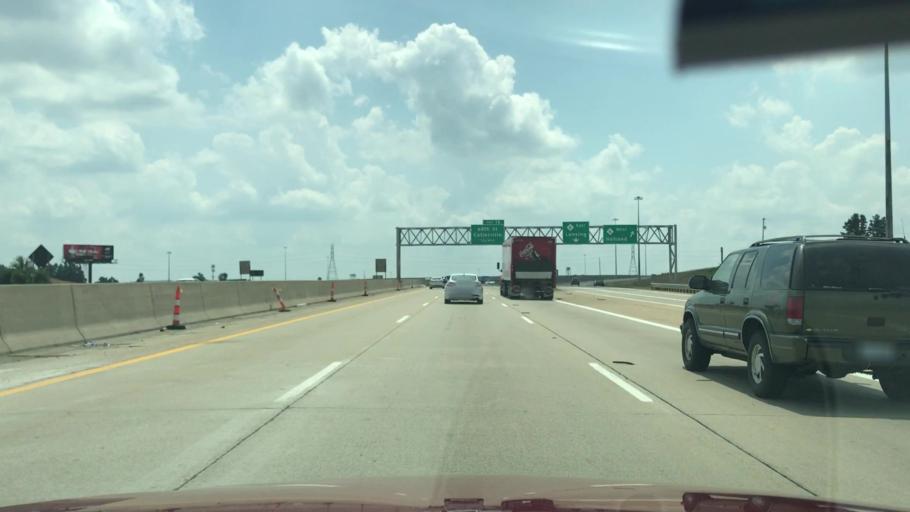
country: US
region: Michigan
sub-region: Kent County
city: Cutlerville
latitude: 42.8561
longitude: -85.6791
